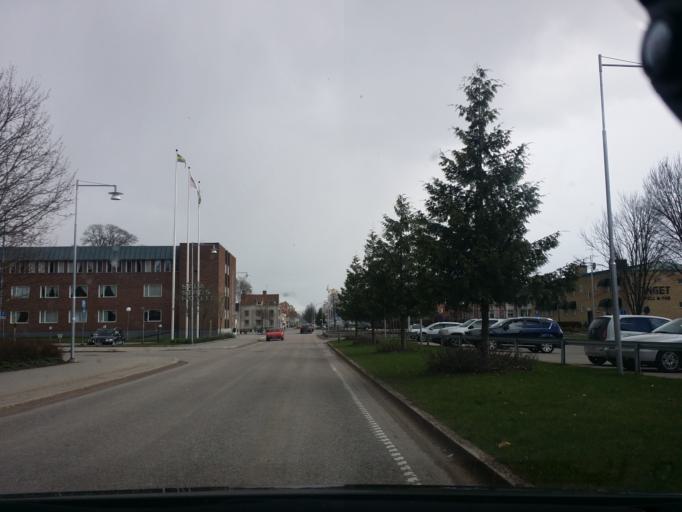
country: SE
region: Vaestmanland
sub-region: Sala Kommun
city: Sala
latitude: 59.9188
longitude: 16.6030
